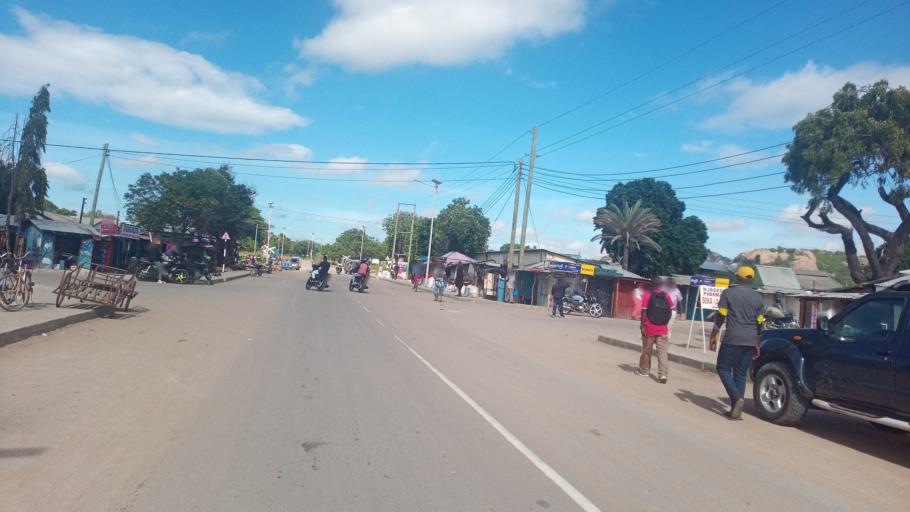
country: TZ
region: Dodoma
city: Dodoma
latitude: -6.1802
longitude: 35.7399
